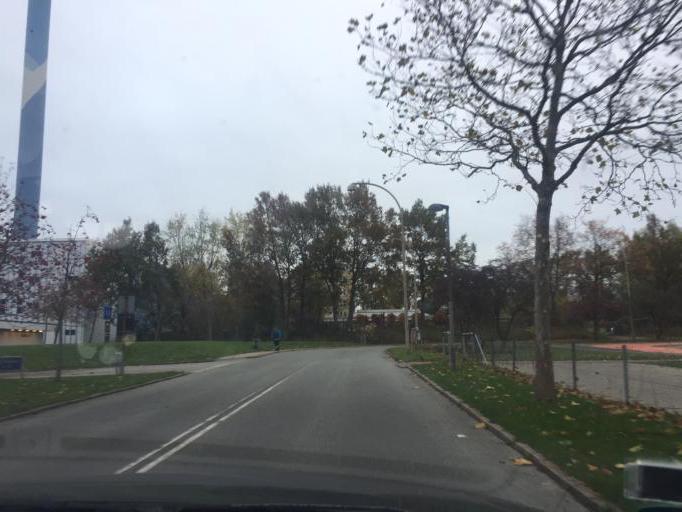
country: DK
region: Capital Region
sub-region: Gladsaxe Municipality
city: Buddinge
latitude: 55.7315
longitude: 12.4867
